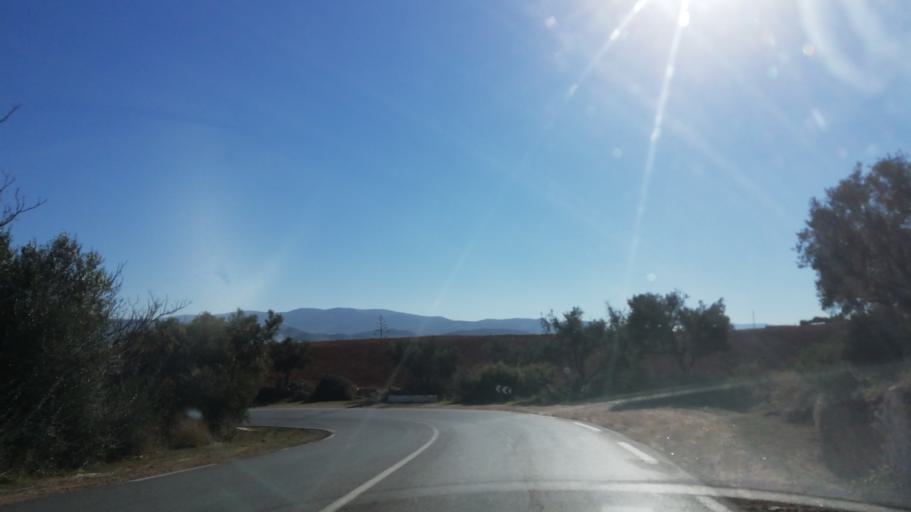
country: DZ
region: Tlemcen
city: Beni Mester
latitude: 34.8281
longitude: -1.5814
